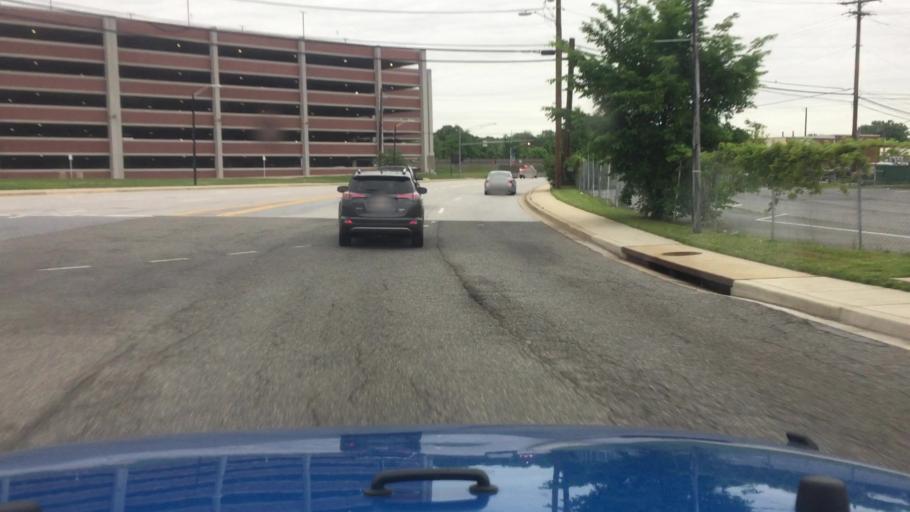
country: US
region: Maryland
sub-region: Prince George's County
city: College Park
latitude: 38.9782
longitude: -76.9263
